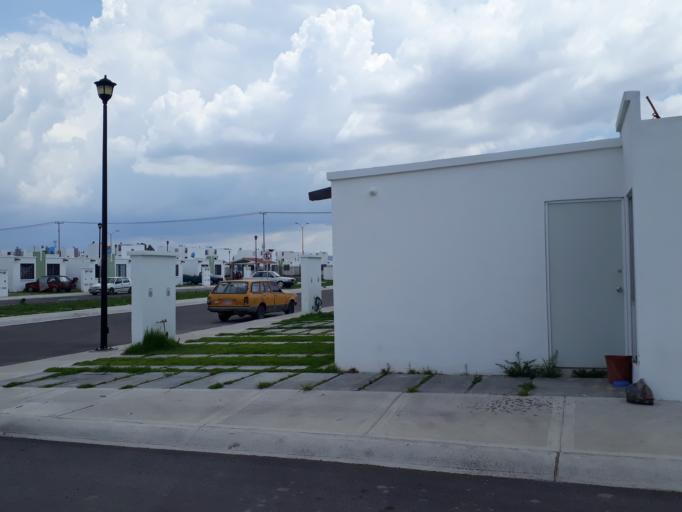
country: MX
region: Aguascalientes
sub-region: Aguascalientes
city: San Sebastian [Fraccionamiento]
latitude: 21.8057
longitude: -102.2738
